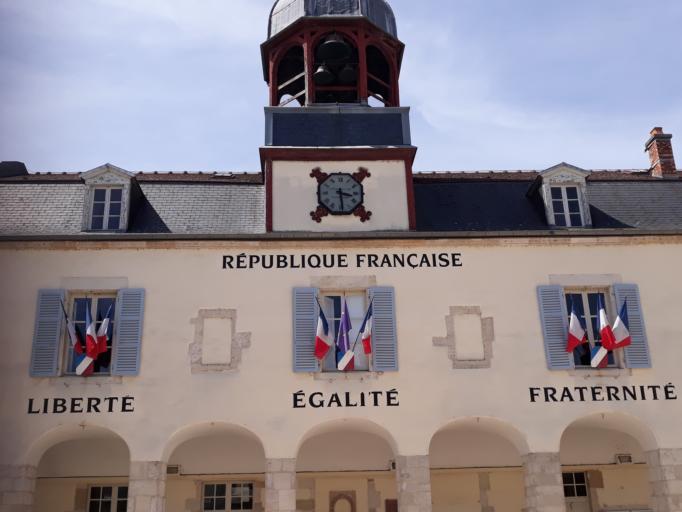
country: FR
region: Champagne-Ardenne
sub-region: Departement de l'Aube
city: Bar-sur-Aube
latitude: 48.2332
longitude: 4.7059
